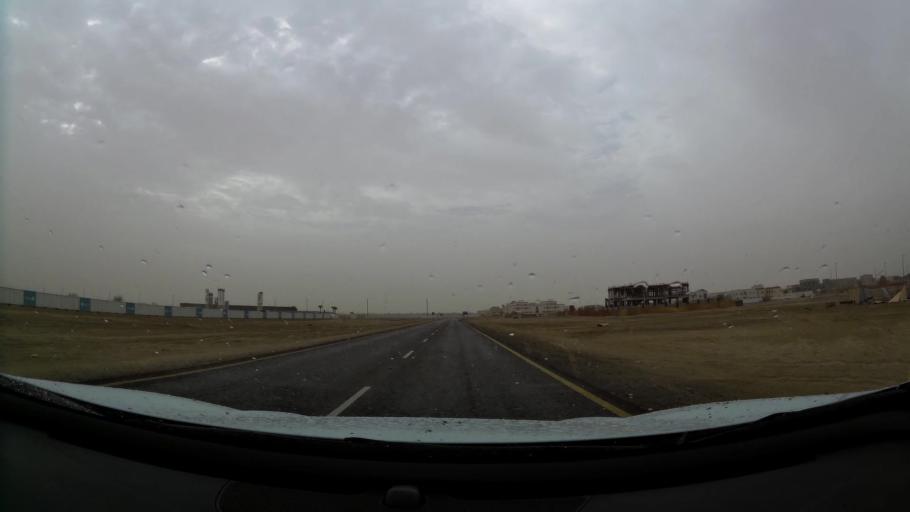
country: AE
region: Abu Dhabi
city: Abu Dhabi
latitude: 24.4193
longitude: 54.6086
